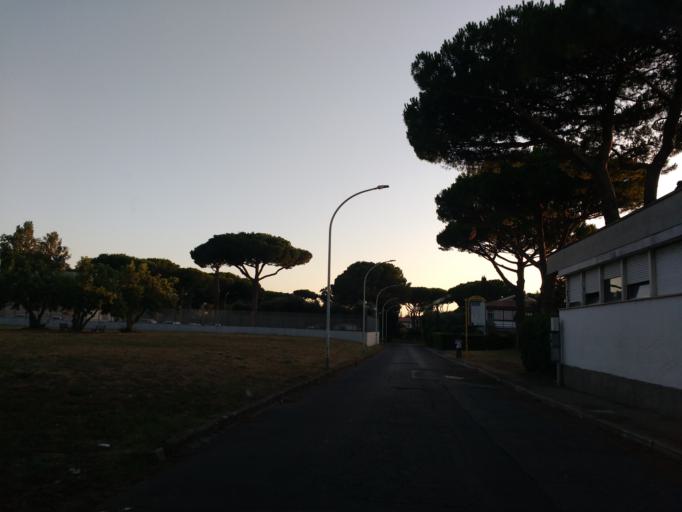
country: IT
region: Latium
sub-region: Citta metropolitana di Roma Capitale
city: Acilia-Castel Fusano-Ostia Antica
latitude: 41.7590
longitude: 12.3611
